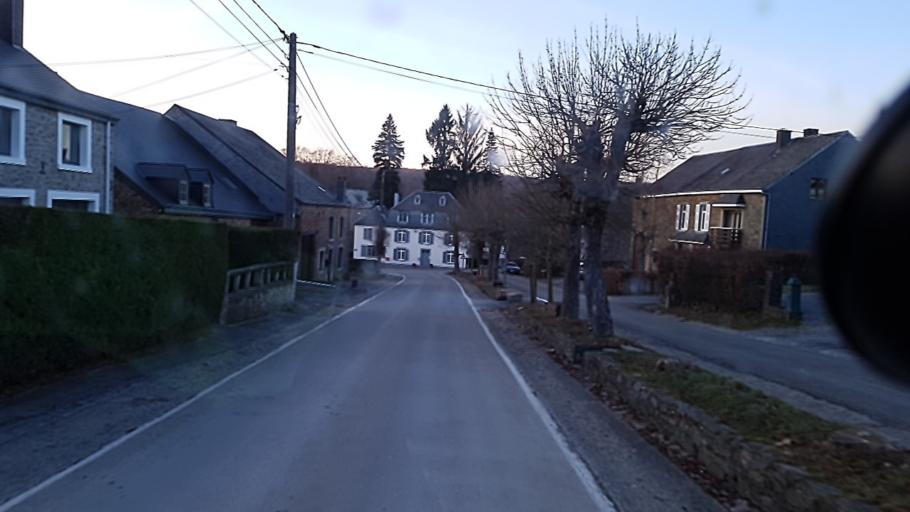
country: BE
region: Wallonia
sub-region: Province du Luxembourg
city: Daverdisse
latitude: 50.0221
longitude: 5.1178
